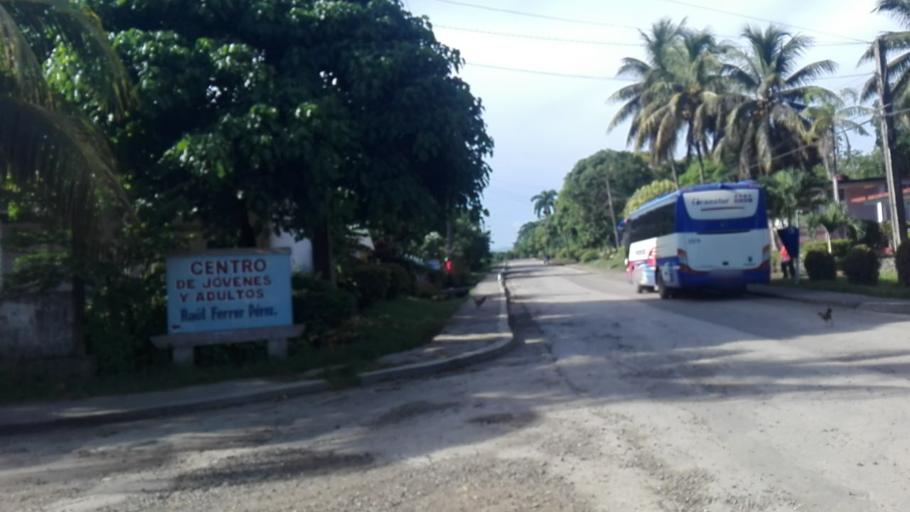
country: CU
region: Granma
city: Bartolome Maso
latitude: 20.1606
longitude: -76.9490
